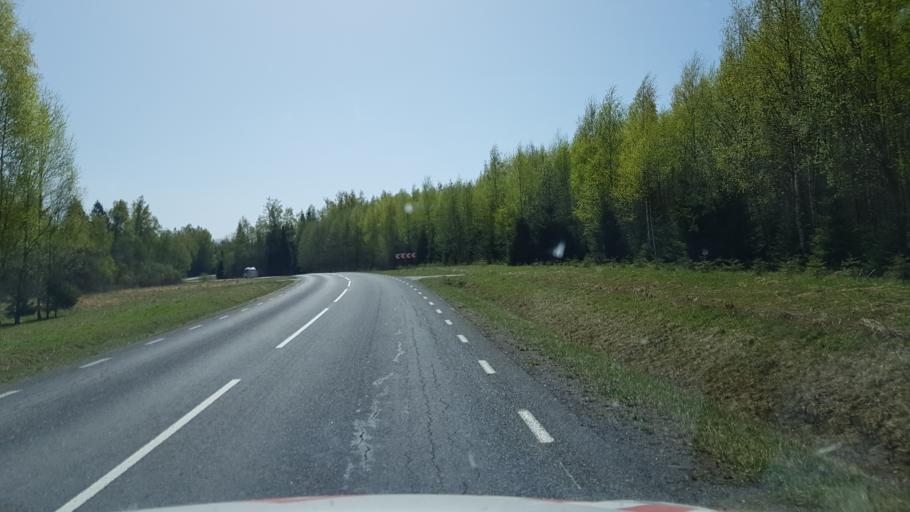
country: EE
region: Viljandimaa
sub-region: Suure-Jaani vald
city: Suure-Jaani
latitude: 58.4839
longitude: 25.4447
